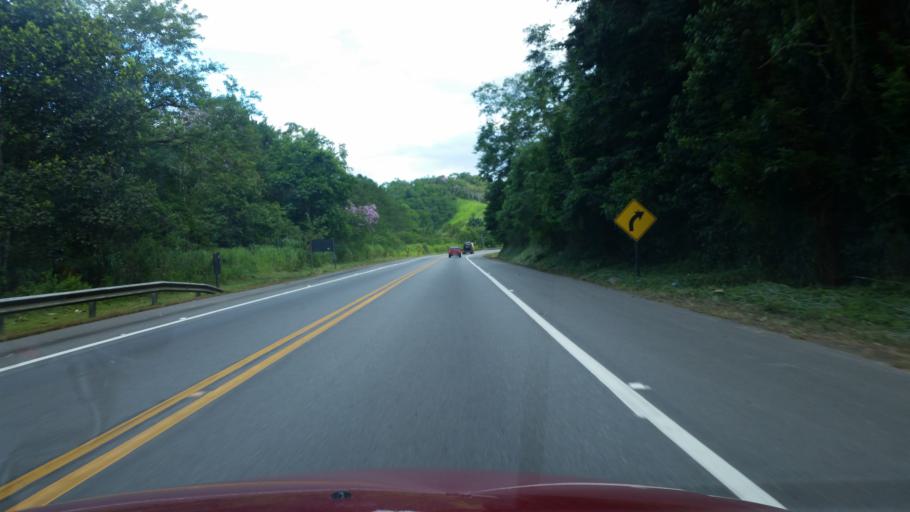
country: BR
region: Sao Paulo
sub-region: Miracatu
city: Miracatu
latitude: -24.2673
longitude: -47.2682
